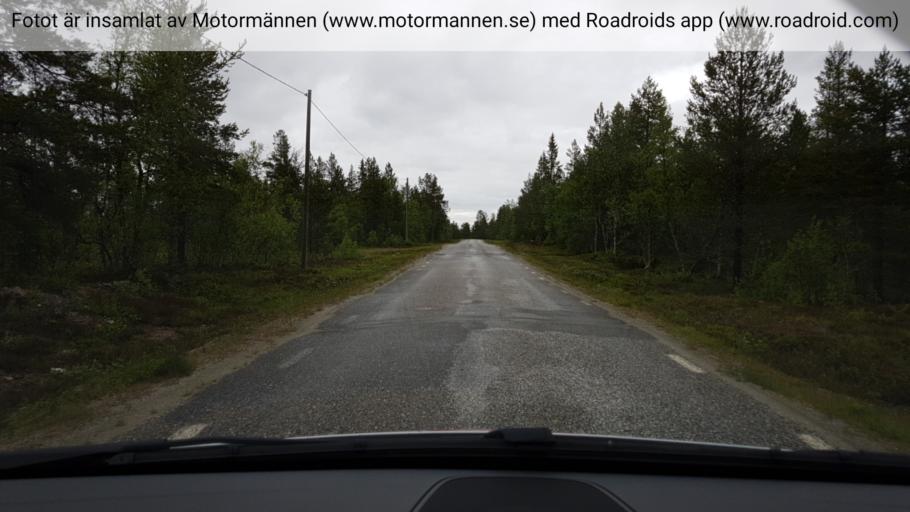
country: SE
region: Jaemtland
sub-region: Harjedalens Kommun
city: Sveg
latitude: 62.3179
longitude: 13.4155
